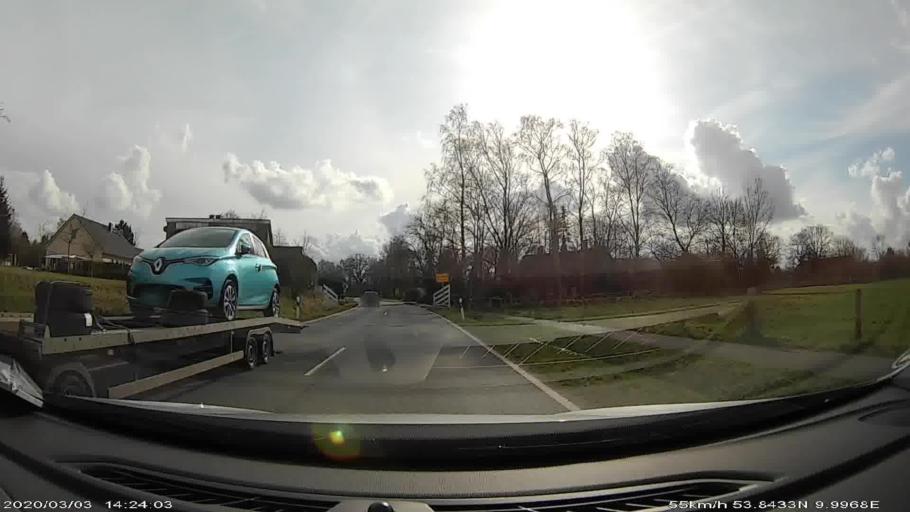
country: DE
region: Schleswig-Holstein
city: Oersdorf
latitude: 53.8432
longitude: 9.9967
